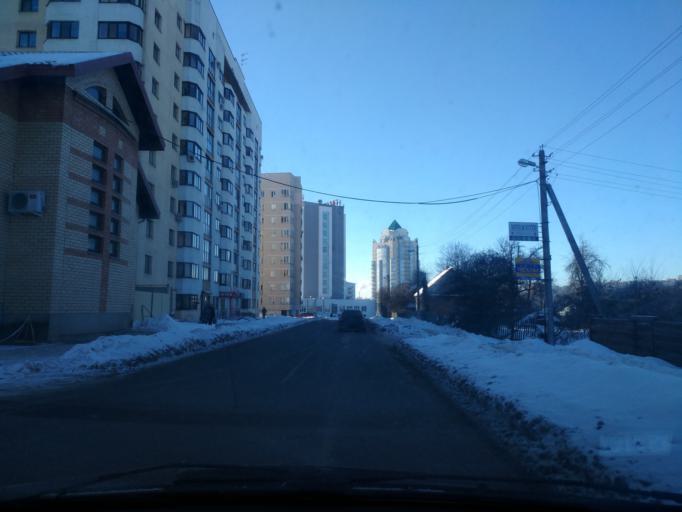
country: BY
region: Mogilev
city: Mahilyow
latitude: 53.9117
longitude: 30.3348
